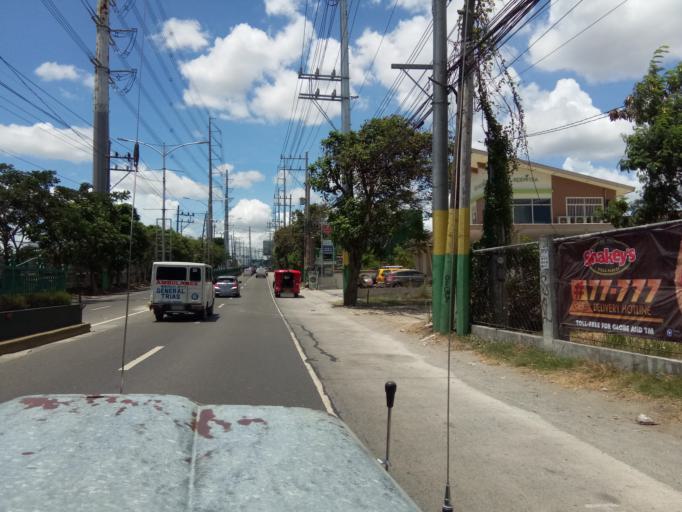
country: PH
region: Calabarzon
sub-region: Province of Cavite
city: Dasmarinas
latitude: 14.3215
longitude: 120.9417
